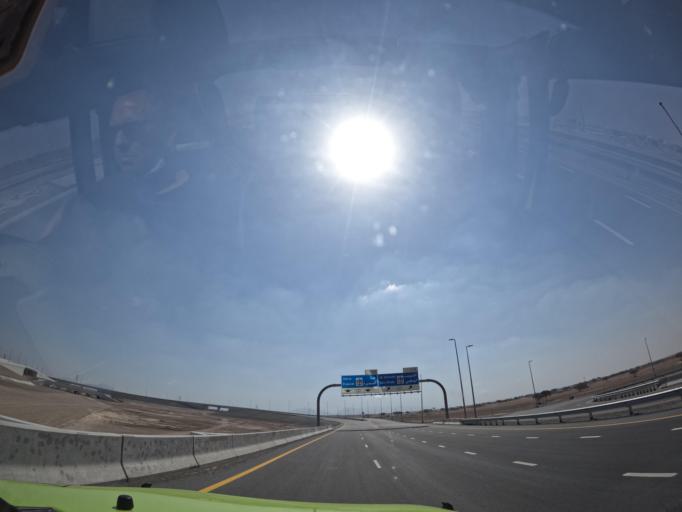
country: AE
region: Ash Shariqah
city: Adh Dhayd
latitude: 24.9103
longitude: 55.7967
